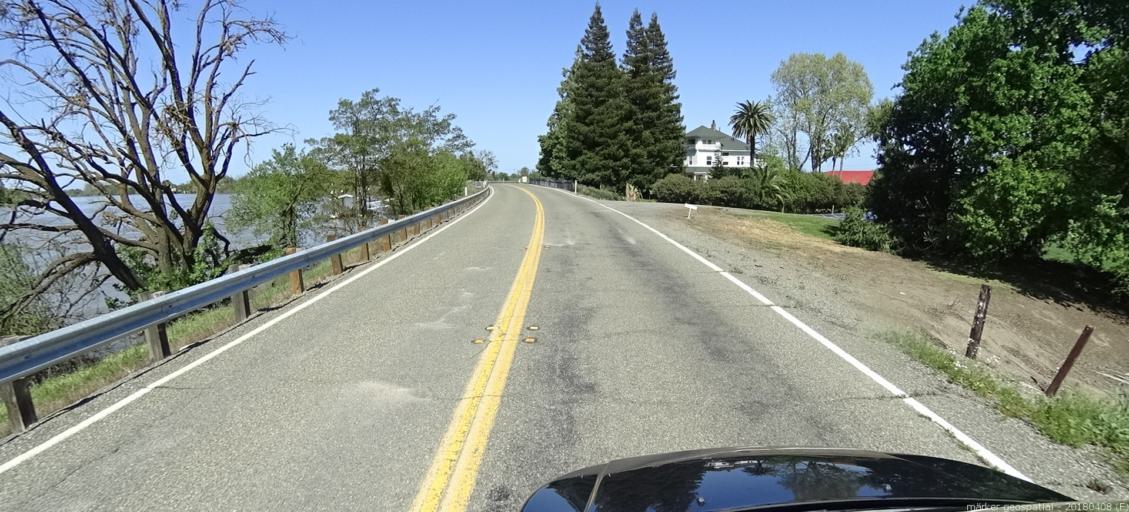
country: US
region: California
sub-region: Sacramento County
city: Laguna
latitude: 38.3599
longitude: -121.5213
